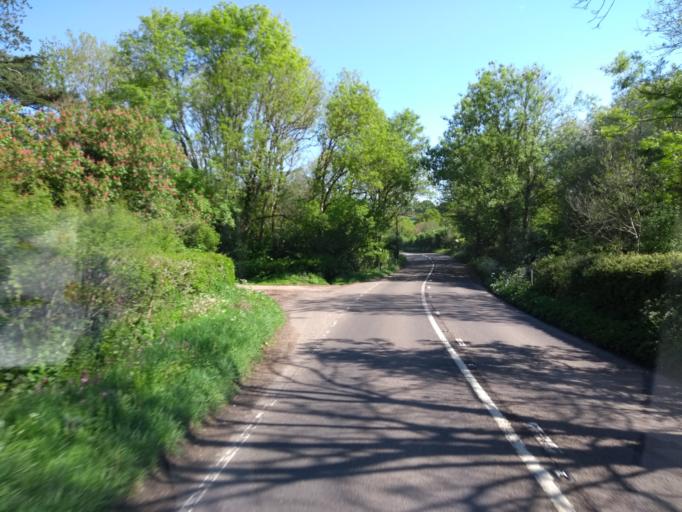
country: GB
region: England
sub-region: Devon
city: Axminster
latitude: 50.8157
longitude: -2.9732
